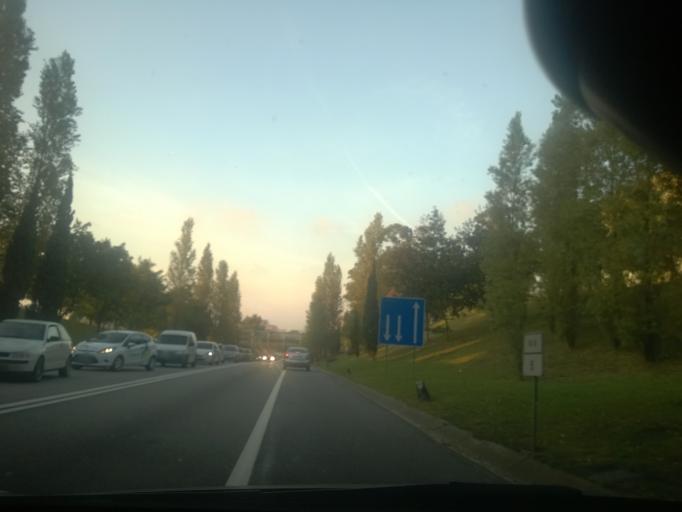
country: PT
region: Porto
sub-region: Maia
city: Maia
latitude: 41.2273
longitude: -8.6263
